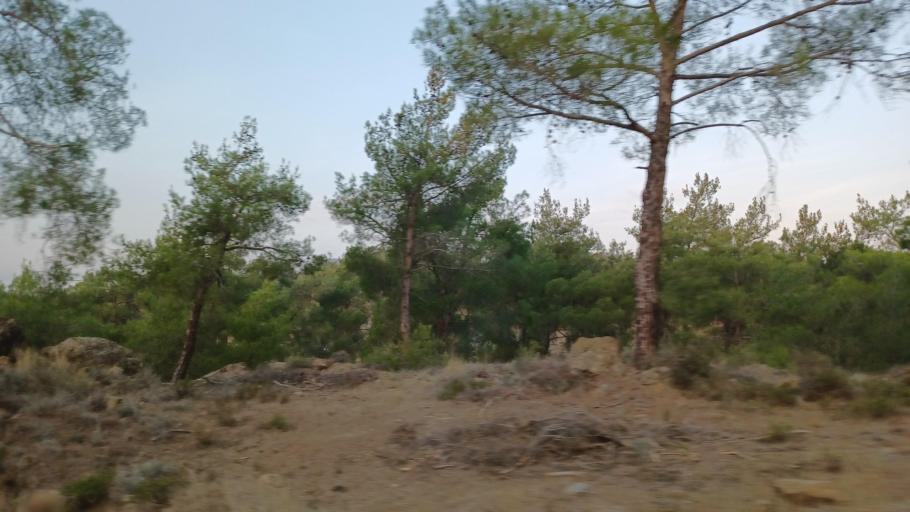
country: CY
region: Larnaka
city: Kornos
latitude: 34.9108
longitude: 33.3578
